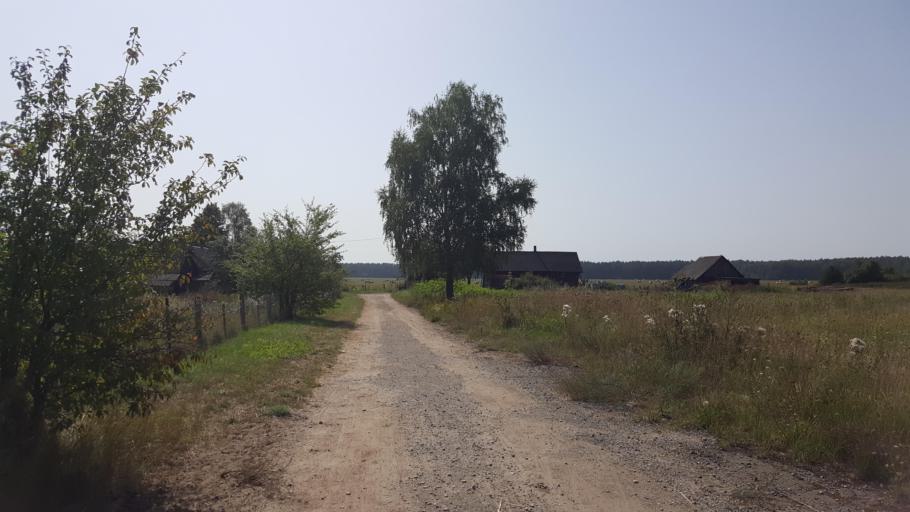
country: BY
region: Brest
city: Pruzhany
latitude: 52.4916
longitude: 24.6064
